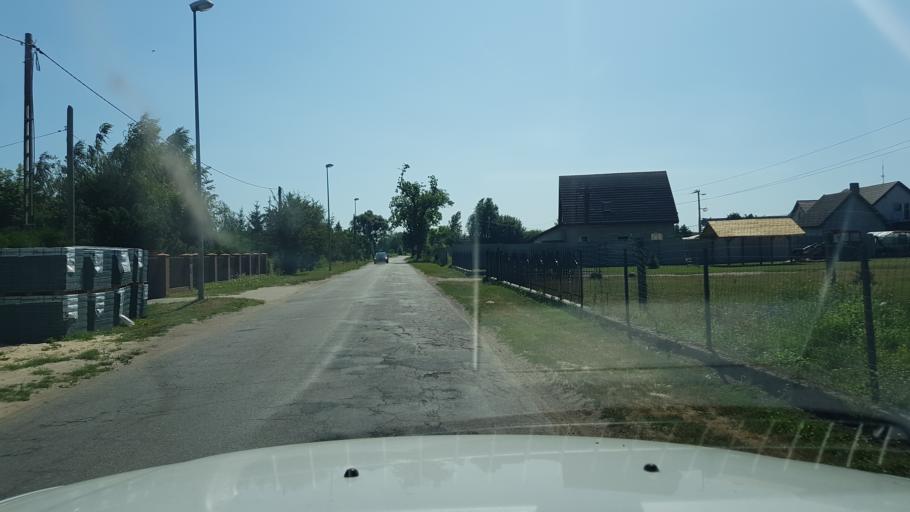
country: PL
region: West Pomeranian Voivodeship
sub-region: Powiat goleniowski
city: Goleniow
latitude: 53.4579
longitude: 14.7238
